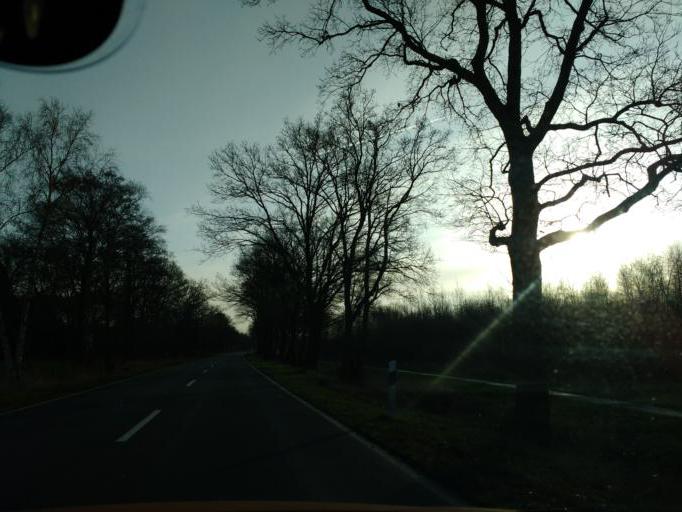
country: DE
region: Lower Saxony
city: Oldenburg
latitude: 53.1352
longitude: 8.2833
